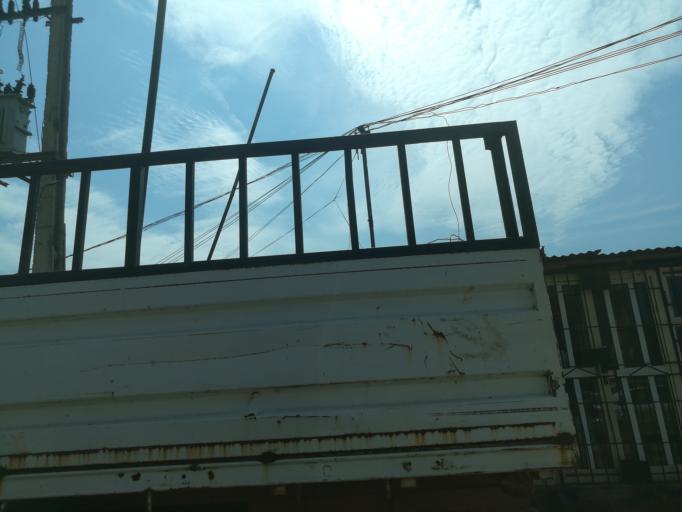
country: NG
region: Lagos
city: Ikorodu
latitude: 6.6278
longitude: 3.4827
